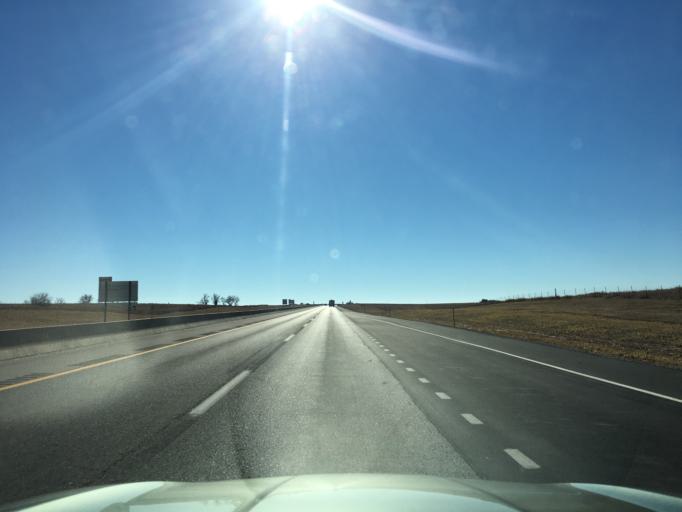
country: US
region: Kansas
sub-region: Sumner County
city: Wellington
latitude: 37.0537
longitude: -97.3384
